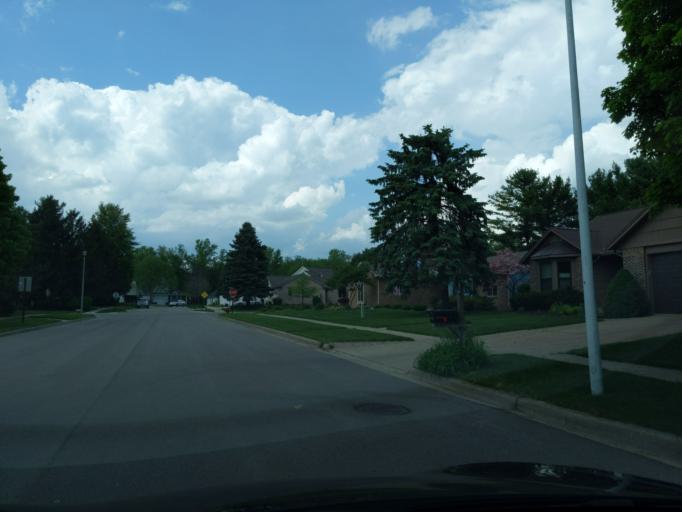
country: US
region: Michigan
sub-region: Ingham County
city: Okemos
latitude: 42.7387
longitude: -84.4316
